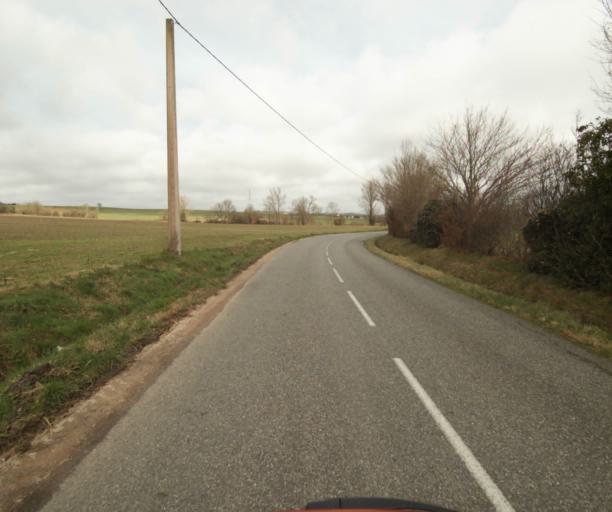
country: FR
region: Midi-Pyrenees
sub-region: Departement de l'Ariege
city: Pamiers
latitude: 43.1144
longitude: 1.5453
